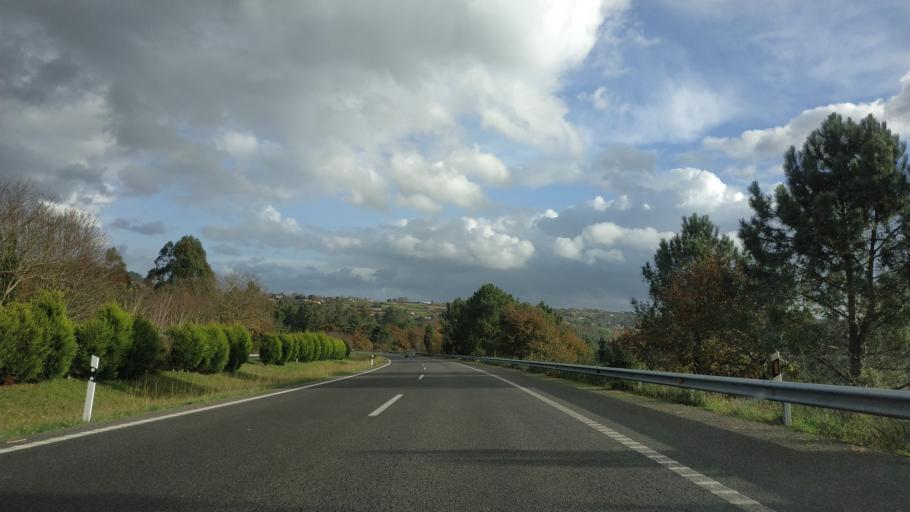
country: ES
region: Galicia
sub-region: Provincia da Coruna
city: Cambre
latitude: 43.2603
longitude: -8.3323
